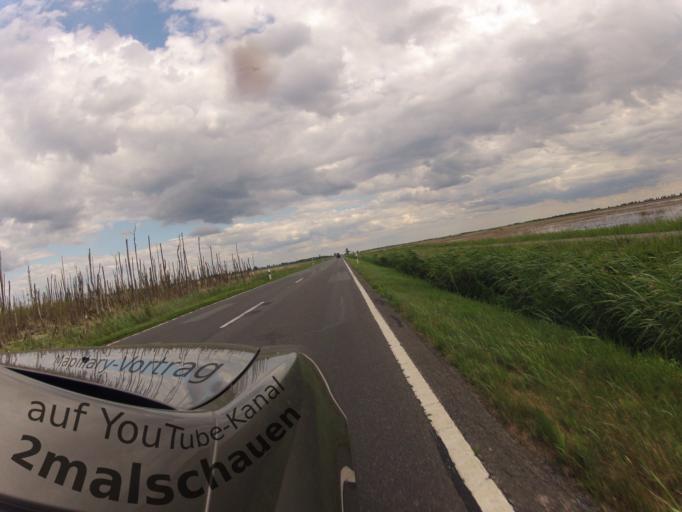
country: DE
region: Mecklenburg-Vorpommern
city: Lassan
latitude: 53.8744
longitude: 13.8063
